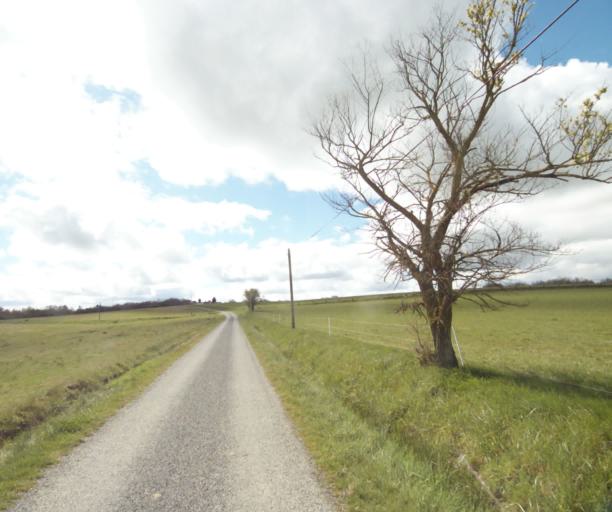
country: FR
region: Midi-Pyrenees
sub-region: Departement de l'Ariege
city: Saverdun
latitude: 43.1843
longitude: 1.5782
